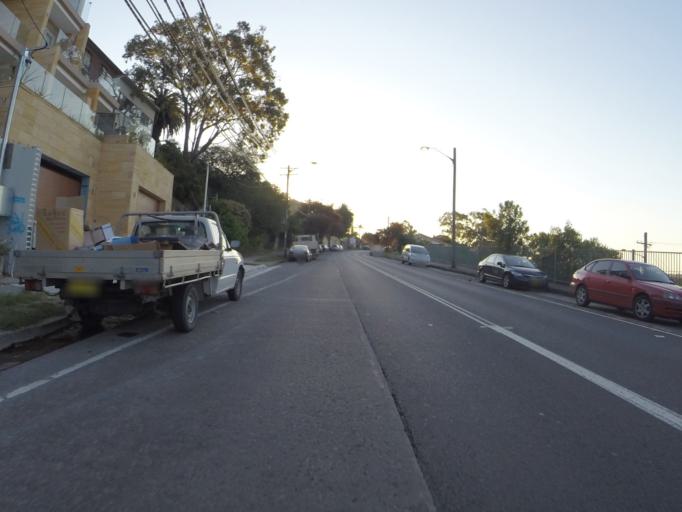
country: AU
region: New South Wales
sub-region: Rockdale
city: Bardwell Valley
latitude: -33.9238
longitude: 151.1411
